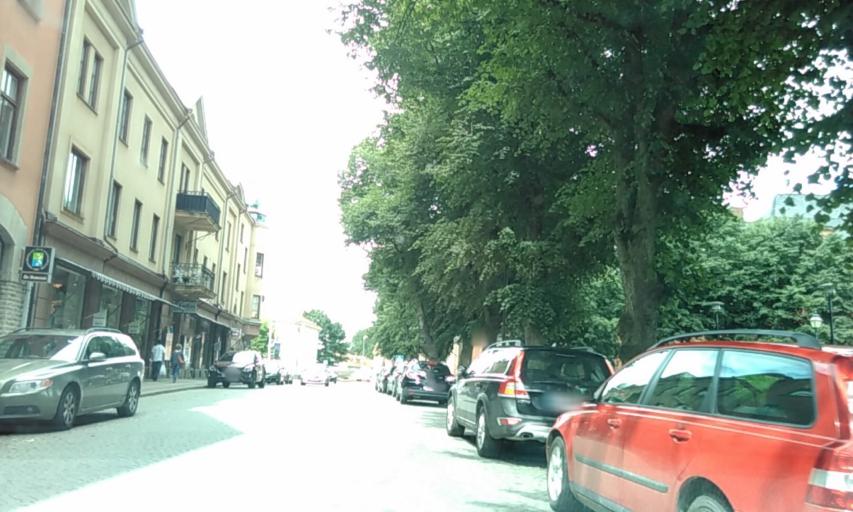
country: SE
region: Vaestra Goetaland
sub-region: Skara Kommun
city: Skara
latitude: 58.3853
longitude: 13.4389
